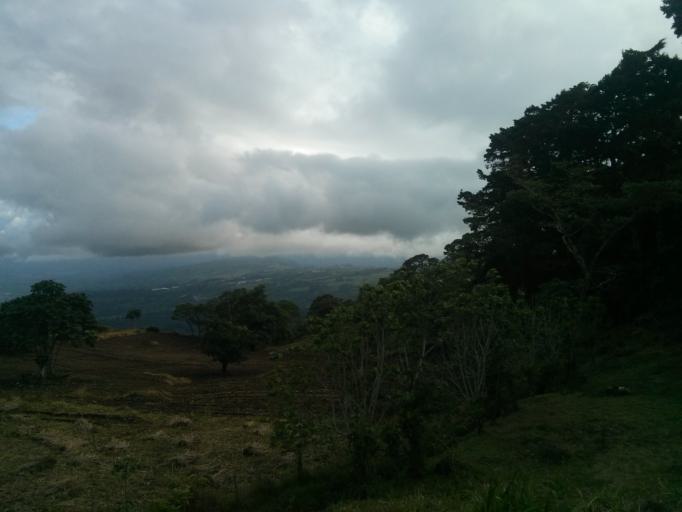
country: CR
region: Cartago
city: Turrialba
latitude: 9.9604
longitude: -83.7498
